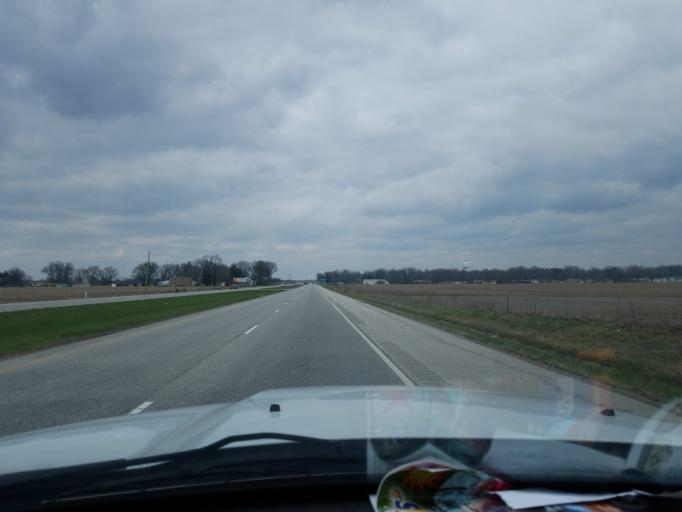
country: US
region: Indiana
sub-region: Sullivan County
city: Farmersburg
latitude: 39.3558
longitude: -87.3879
